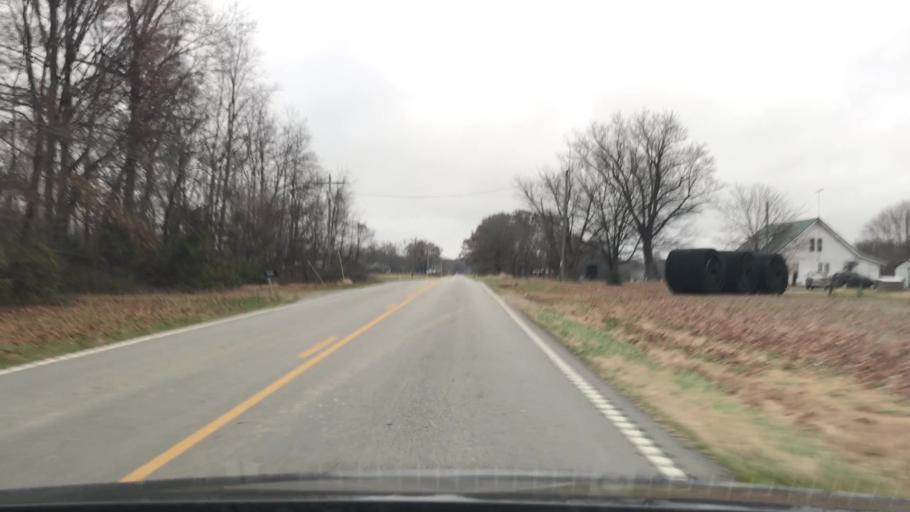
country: US
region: Kentucky
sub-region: Todd County
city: Guthrie
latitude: 36.7157
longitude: -87.1921
